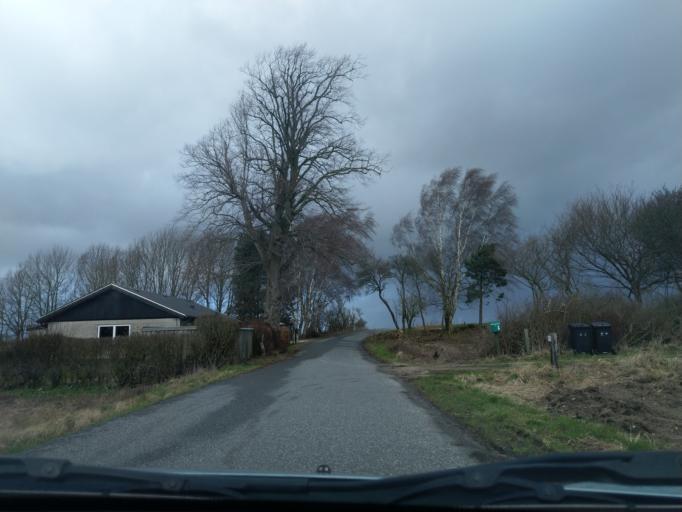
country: DK
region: Zealand
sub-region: Naestved Kommune
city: Fuglebjerg
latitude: 55.3461
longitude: 11.5834
